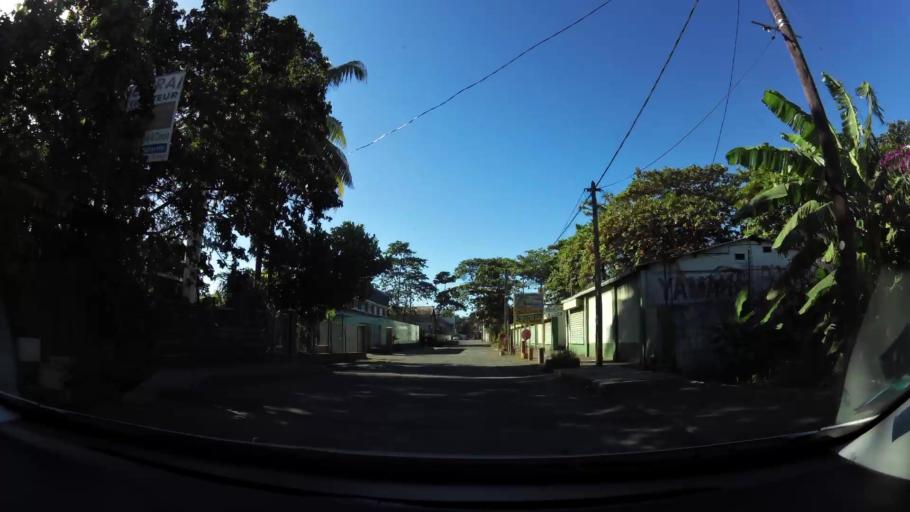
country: YT
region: Mamoudzou
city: Mamoudzou
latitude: -12.7699
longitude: 45.2257
